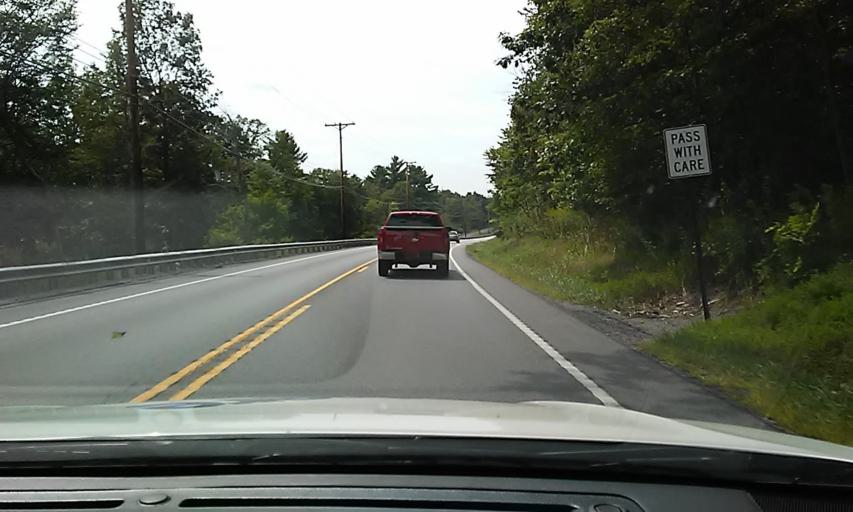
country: US
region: Pennsylvania
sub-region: Clearfield County
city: Treasure Lake
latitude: 41.1486
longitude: -78.6711
